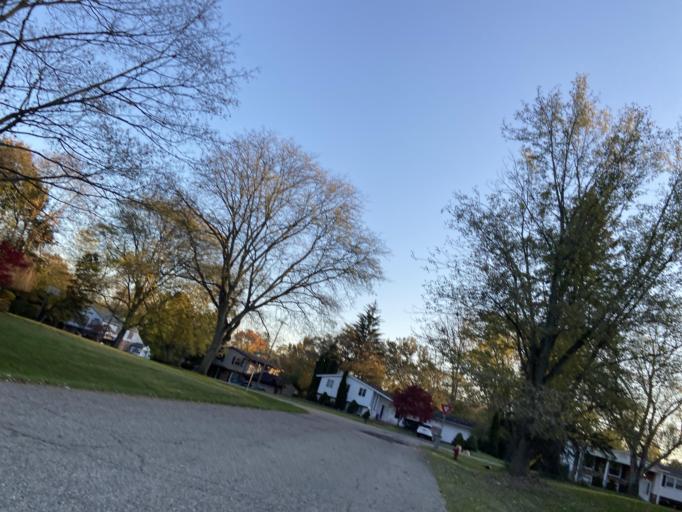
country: US
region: Michigan
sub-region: Oakland County
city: Franklin
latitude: 42.5324
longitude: -83.3364
